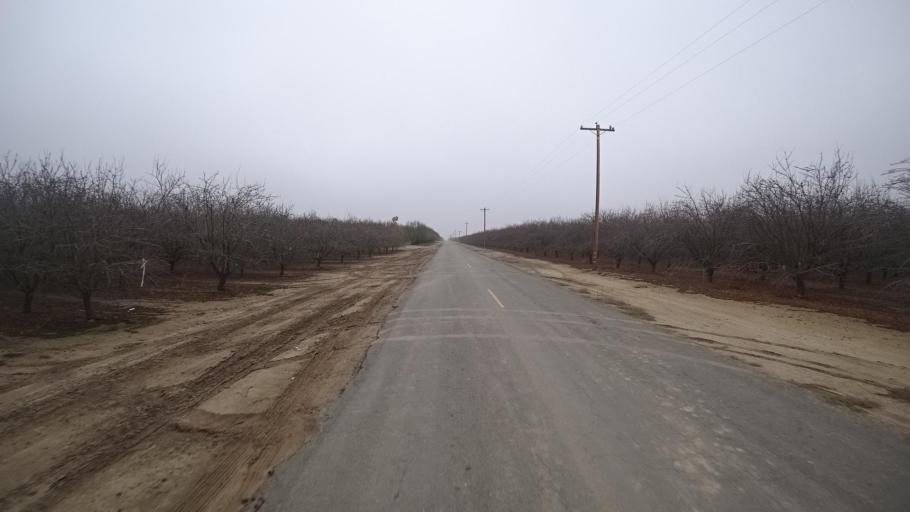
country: US
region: California
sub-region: Kern County
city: Wasco
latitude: 35.5927
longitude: -119.5092
